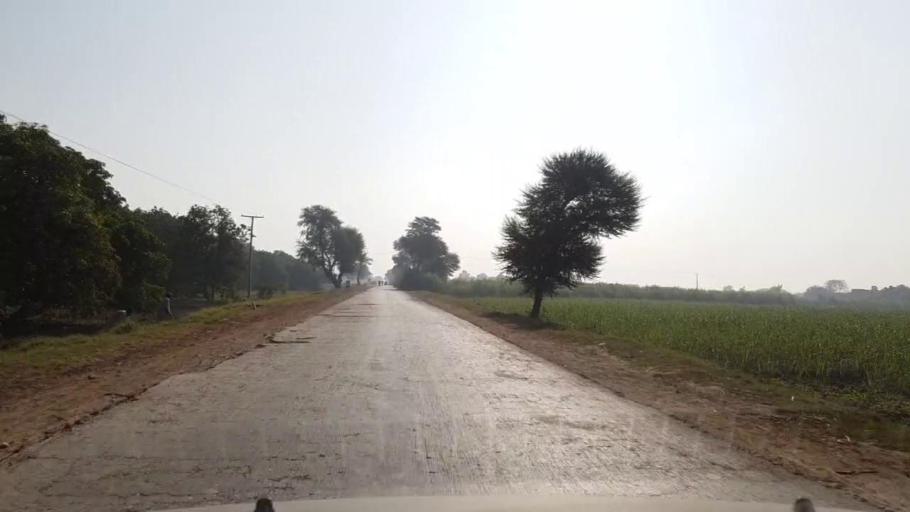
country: PK
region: Sindh
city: Matiari
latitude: 25.5592
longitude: 68.5302
